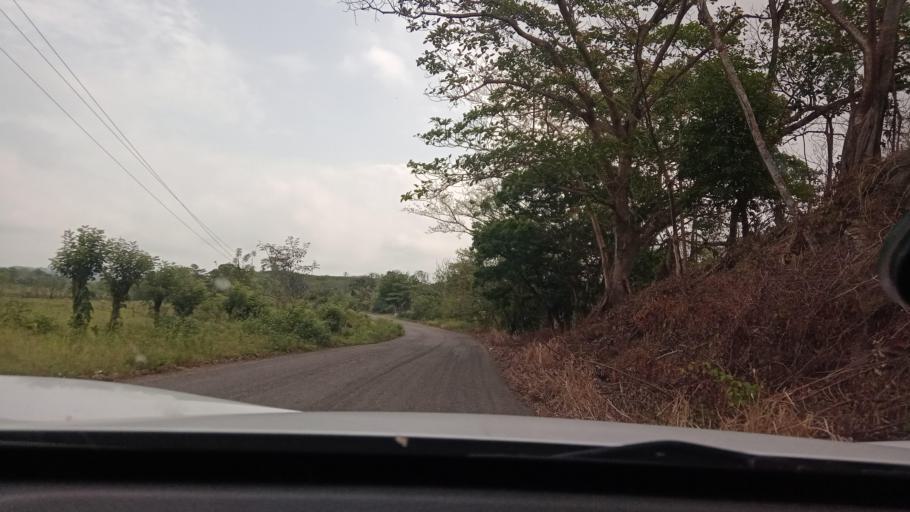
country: MX
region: Tabasco
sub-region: Huimanguillo
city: Francisco Rueda
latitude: 17.5466
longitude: -94.1284
